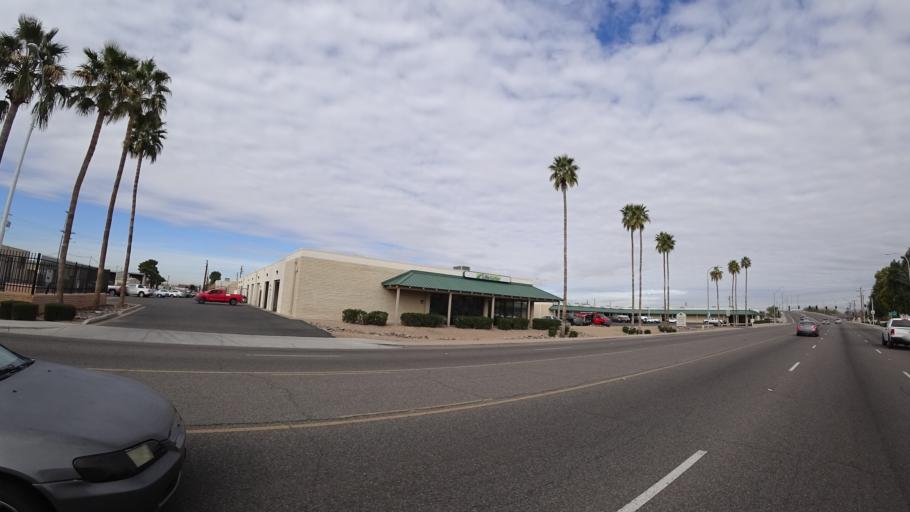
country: US
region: Arizona
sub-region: Maricopa County
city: Glendale
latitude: 33.5185
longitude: -112.1687
